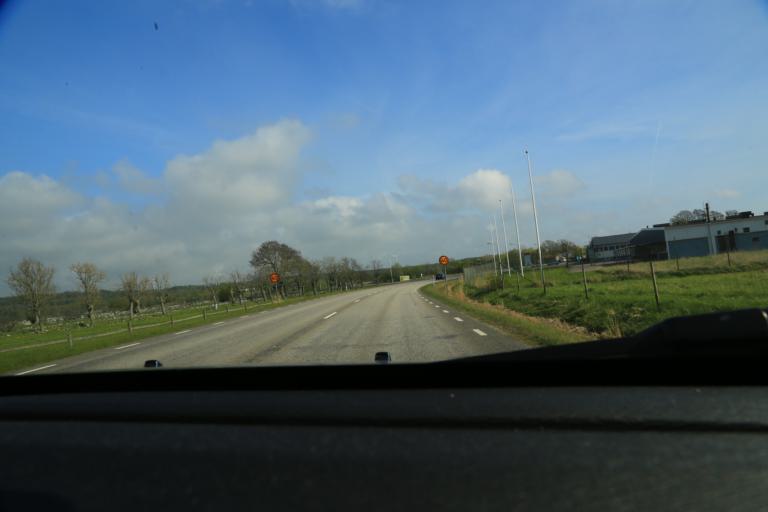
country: SE
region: Halland
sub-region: Varbergs Kommun
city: Veddige
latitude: 57.2236
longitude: 12.2200
